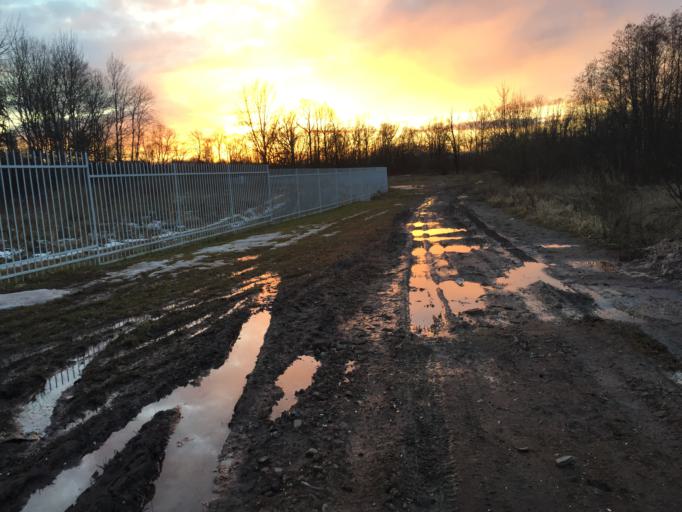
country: RU
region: St.-Petersburg
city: Pushkin
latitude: 59.7264
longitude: 30.3771
